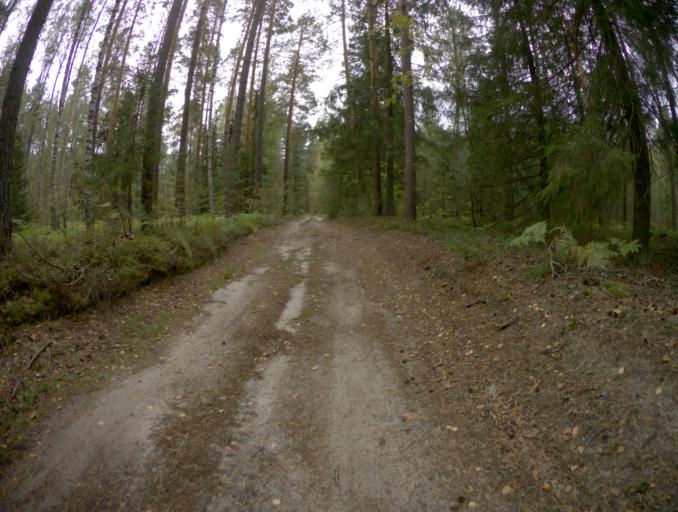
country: RU
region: Vladimir
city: Ivanishchi
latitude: 55.8464
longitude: 40.3441
